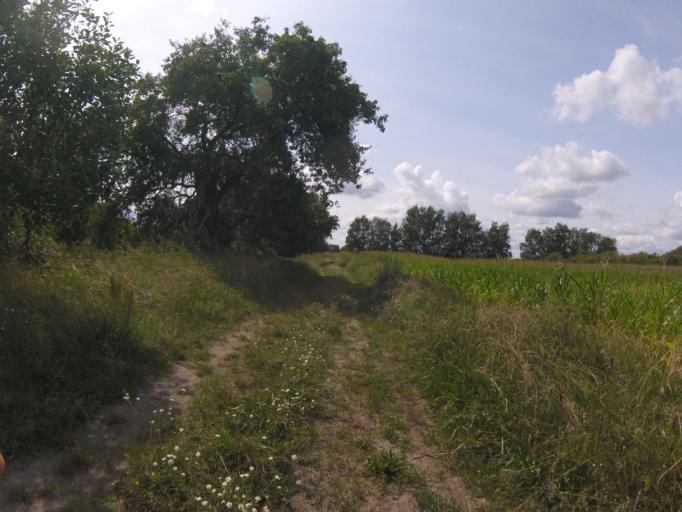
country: DE
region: Brandenburg
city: Mittenwalde
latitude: 52.2872
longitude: 13.5058
